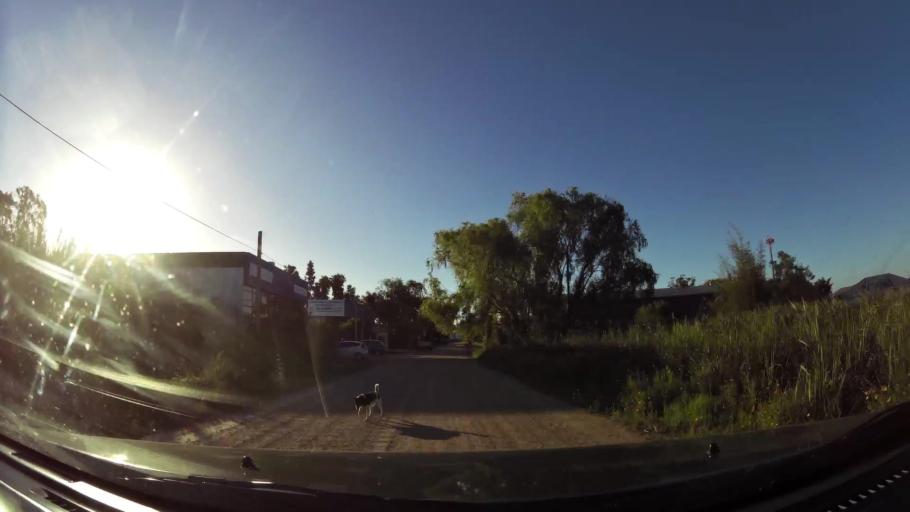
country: UY
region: Canelones
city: Paso de Carrasco
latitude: -34.8487
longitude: -56.0259
